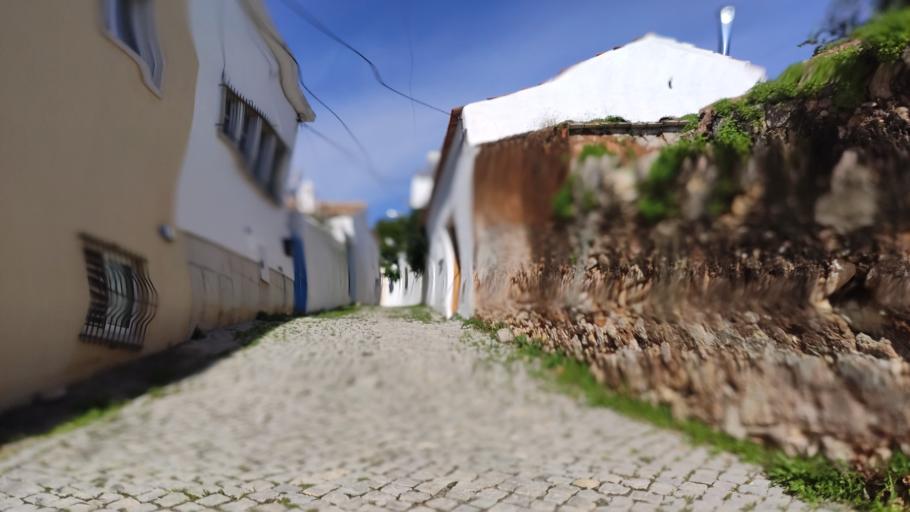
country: PT
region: Faro
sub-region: Sao Bras de Alportel
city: Sao Bras de Alportel
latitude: 37.1502
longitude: -7.8878
